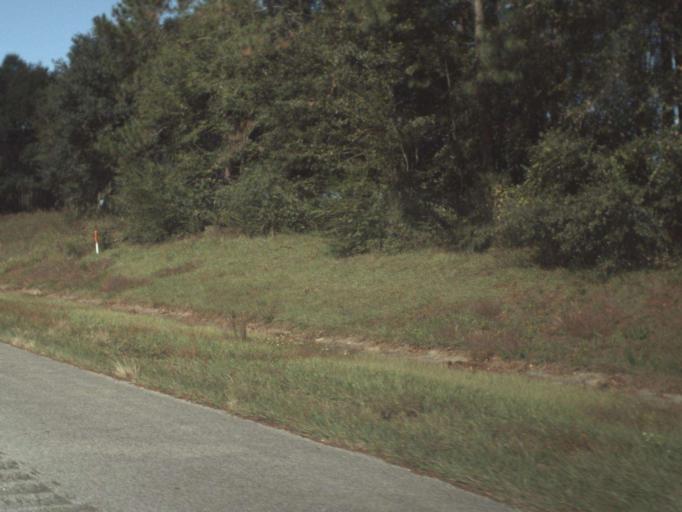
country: US
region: Florida
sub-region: Washington County
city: Chipley
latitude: 30.7505
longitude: -85.5656
